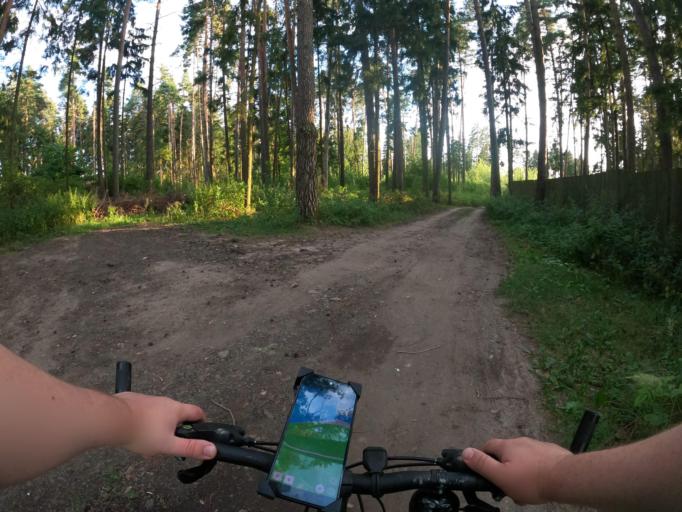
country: RU
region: Moskovskaya
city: Malyshevo
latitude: 55.5562
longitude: 38.3324
